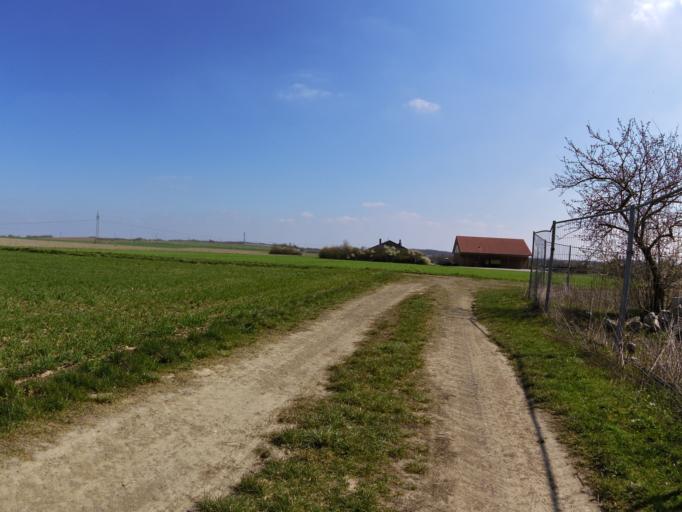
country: DE
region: Bavaria
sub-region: Regierungsbezirk Unterfranken
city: Biebelried
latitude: 49.7353
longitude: 10.0834
